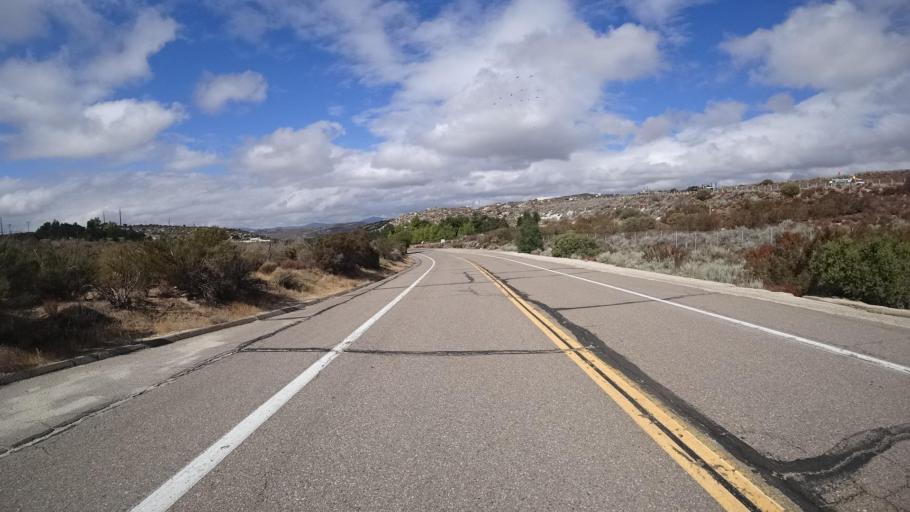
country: US
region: California
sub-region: San Diego County
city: Campo
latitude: 32.7040
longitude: -116.3611
